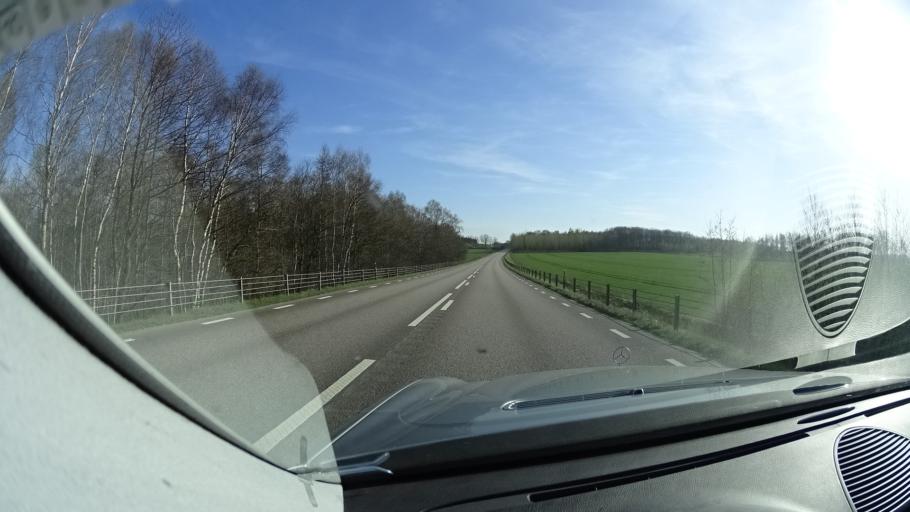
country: SE
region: Skane
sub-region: Bjuvs Kommun
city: Billesholm
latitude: 56.0272
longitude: 12.9662
